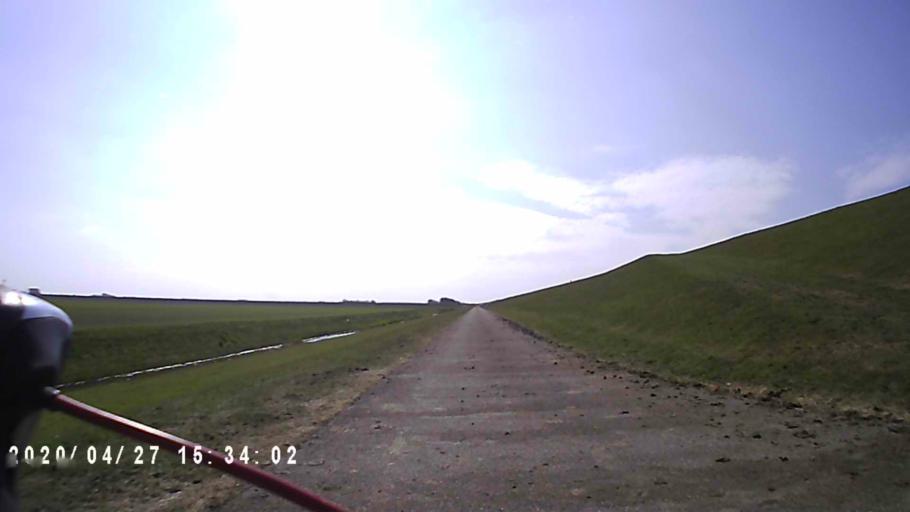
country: NL
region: Groningen
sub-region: Gemeente De Marne
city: Ulrum
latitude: 53.4001
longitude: 6.3373
